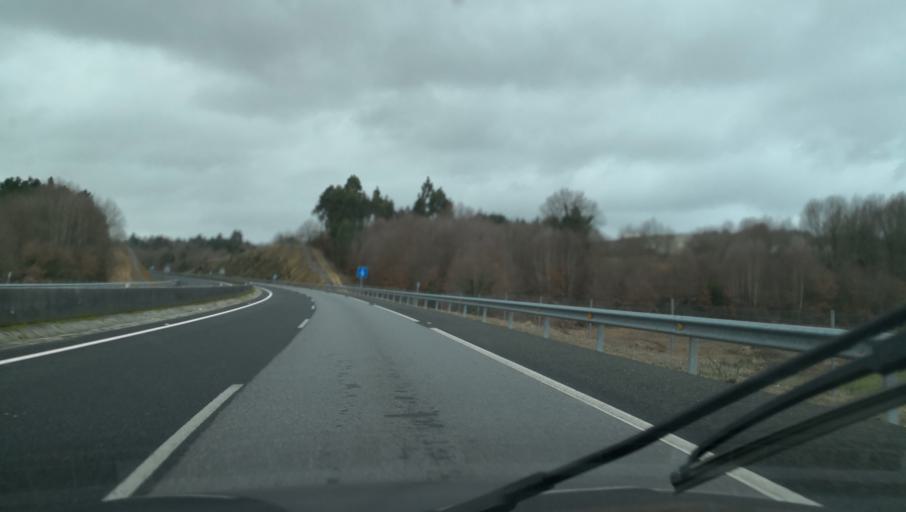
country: ES
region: Galicia
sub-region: Provincia de Pontevedra
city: Lalin
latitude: 42.6693
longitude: -8.1498
